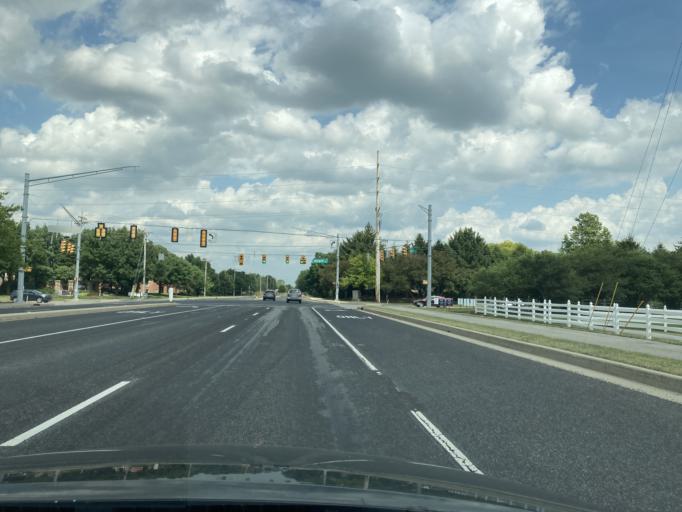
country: US
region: Indiana
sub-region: Hamilton County
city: Carmel
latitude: 39.9994
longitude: -86.1656
